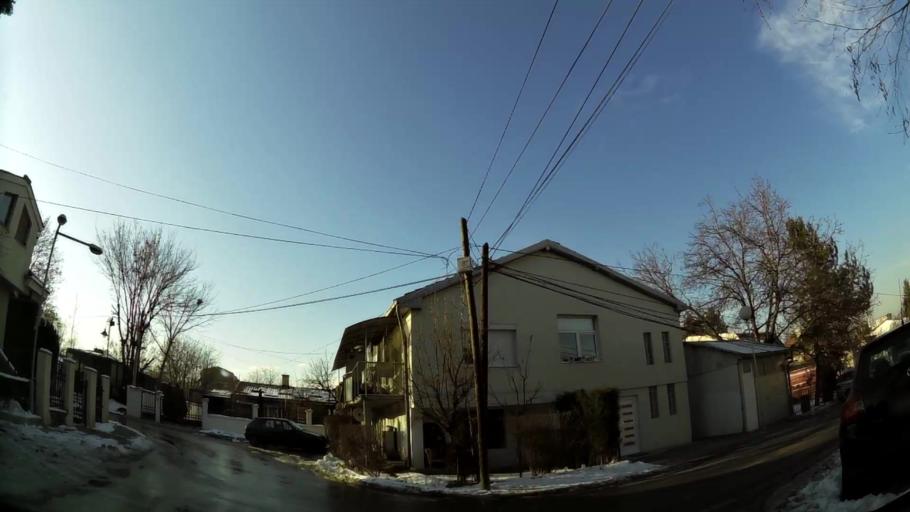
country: MK
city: Krushopek
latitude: 41.9999
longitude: 21.3837
